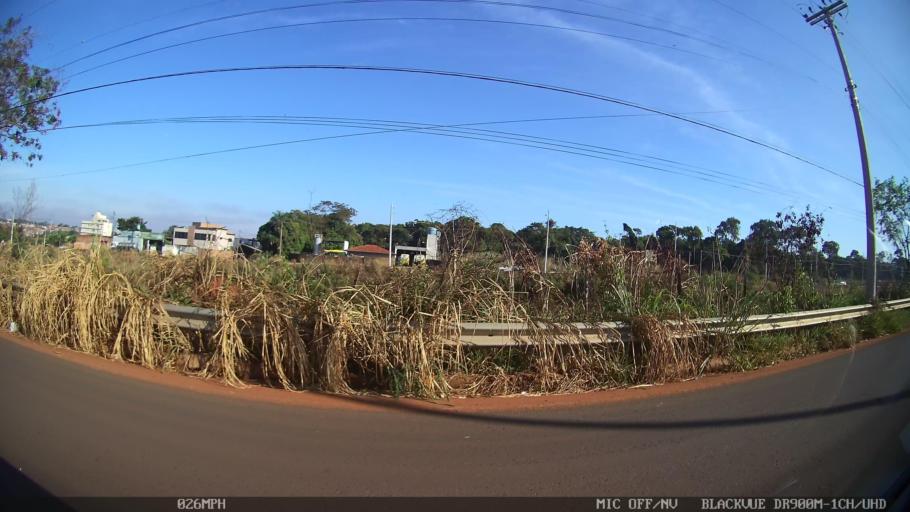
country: BR
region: Sao Paulo
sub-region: Sao Jose Do Rio Preto
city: Sao Jose do Rio Preto
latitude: -20.7703
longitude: -49.3496
